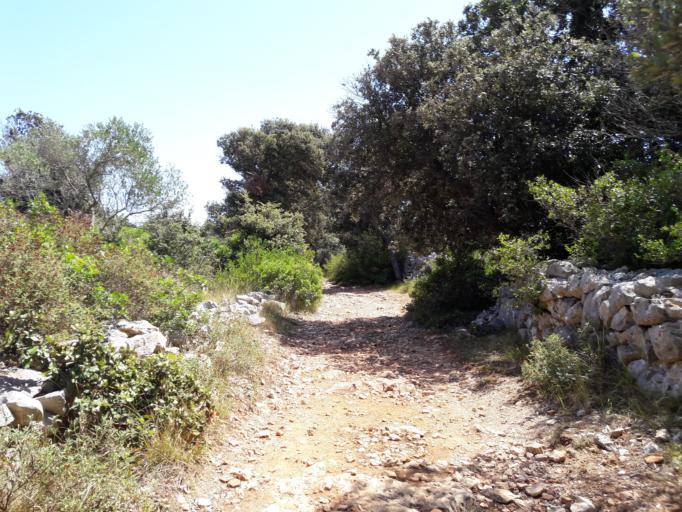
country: HR
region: Licko-Senjska
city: Novalja
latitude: 44.3674
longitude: 14.6985
